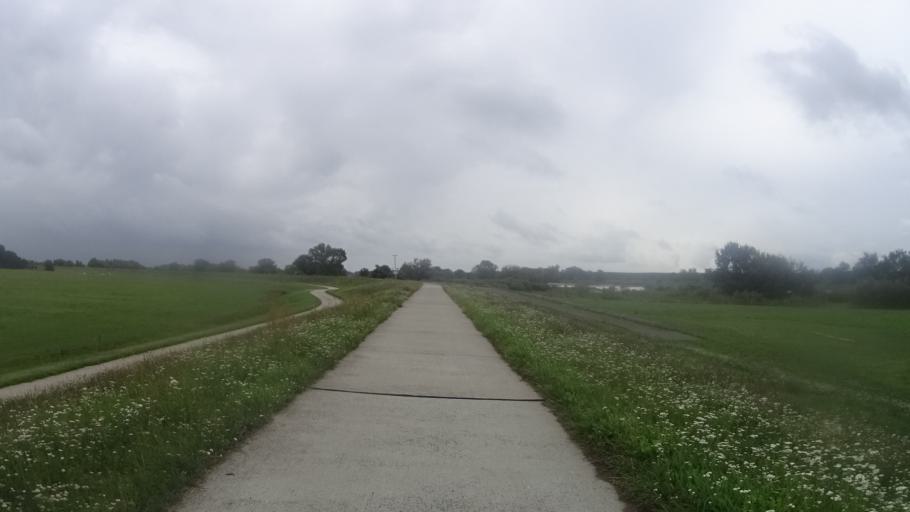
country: DE
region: Lower Saxony
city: Bleckede
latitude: 53.2963
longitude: 10.7630
